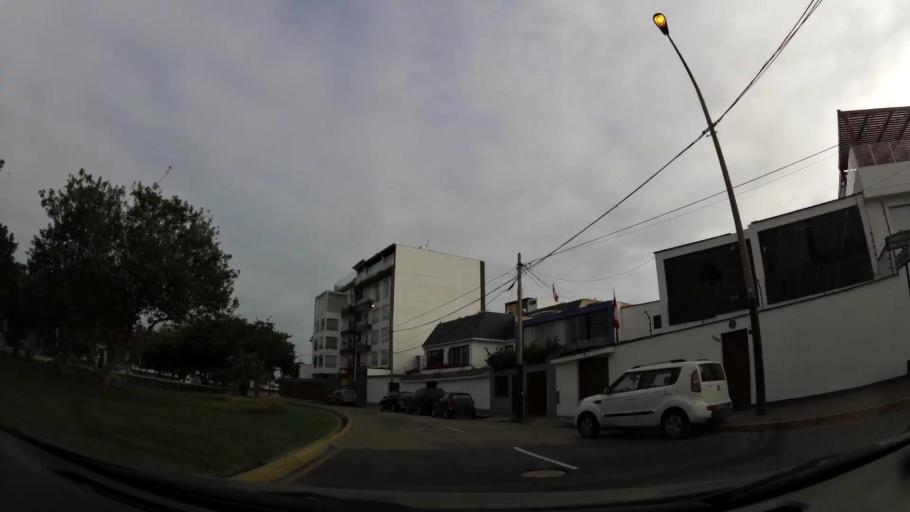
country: PE
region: Lima
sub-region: Lima
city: San Isidro
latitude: -12.1044
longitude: -77.0598
